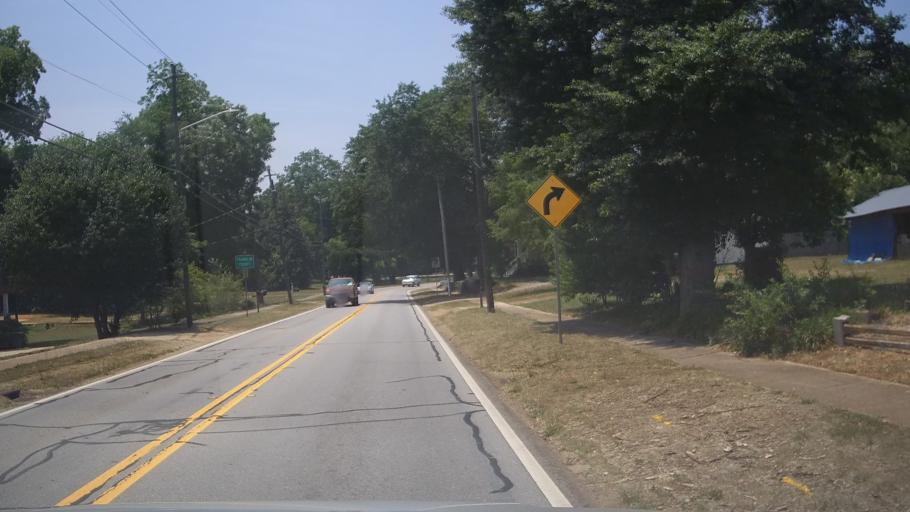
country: US
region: Georgia
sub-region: Hart County
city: Royston
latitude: 34.2872
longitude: -83.1038
